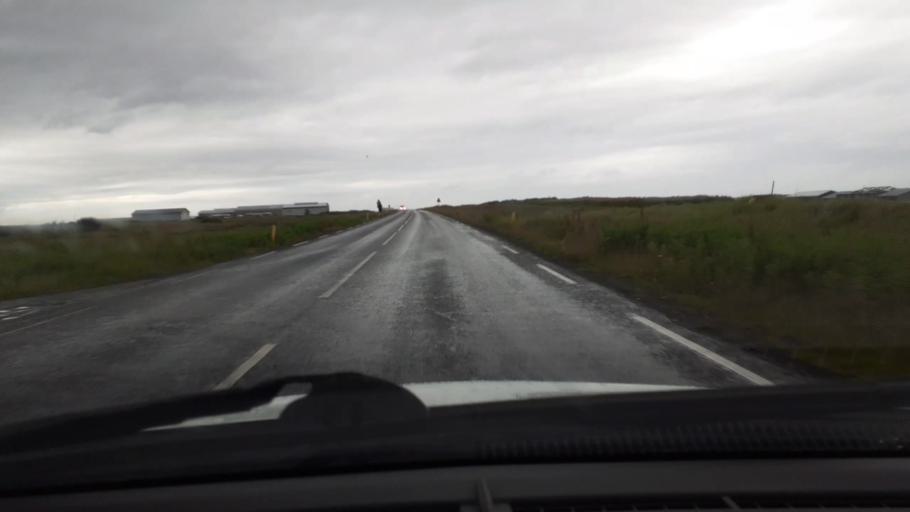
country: IS
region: West
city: Akranes
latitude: 64.3429
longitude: -22.0147
